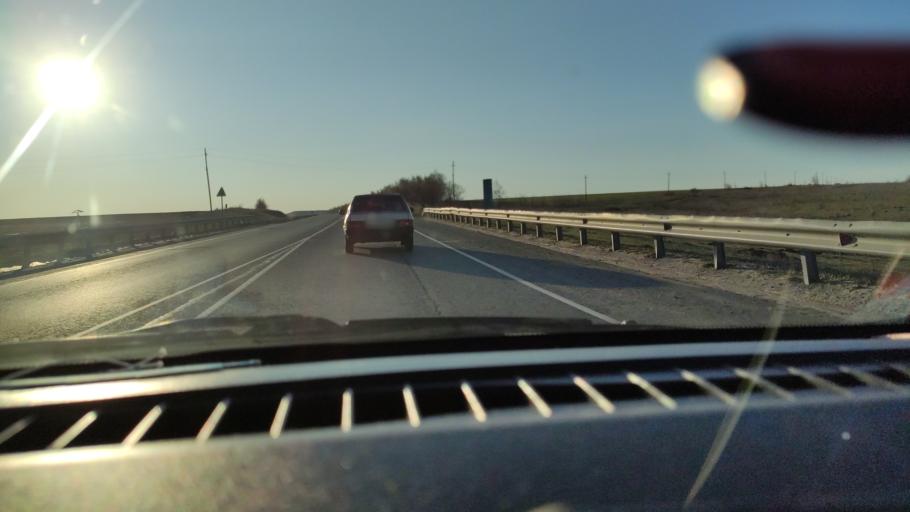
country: RU
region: Saratov
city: Shikhany
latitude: 52.1170
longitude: 47.2804
